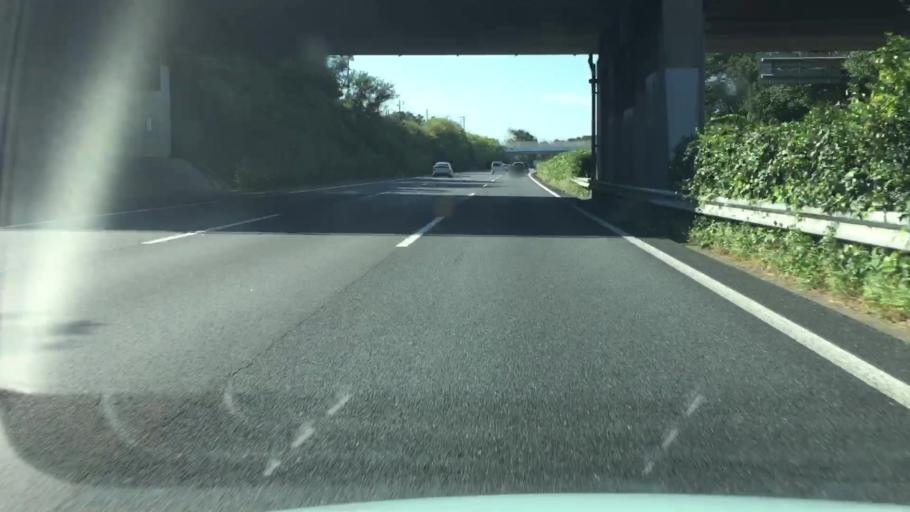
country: JP
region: Ibaraki
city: Ishioka
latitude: 36.2138
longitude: 140.2751
